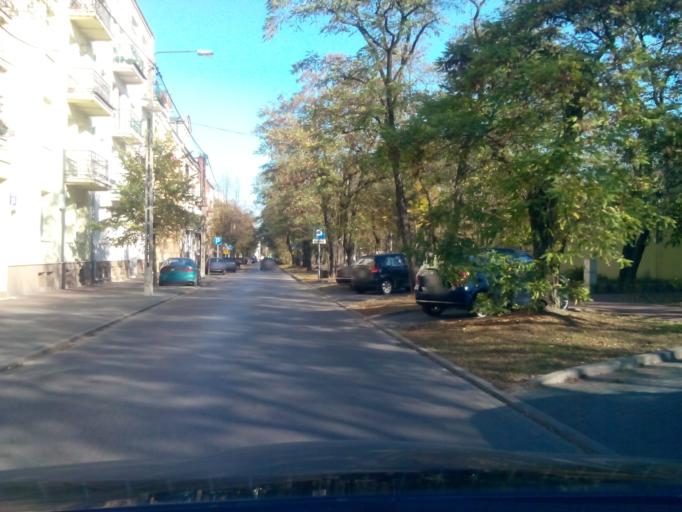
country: PL
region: Masovian Voivodeship
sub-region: Powiat pruszkowski
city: Pruszkow
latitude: 52.1647
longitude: 20.8002
